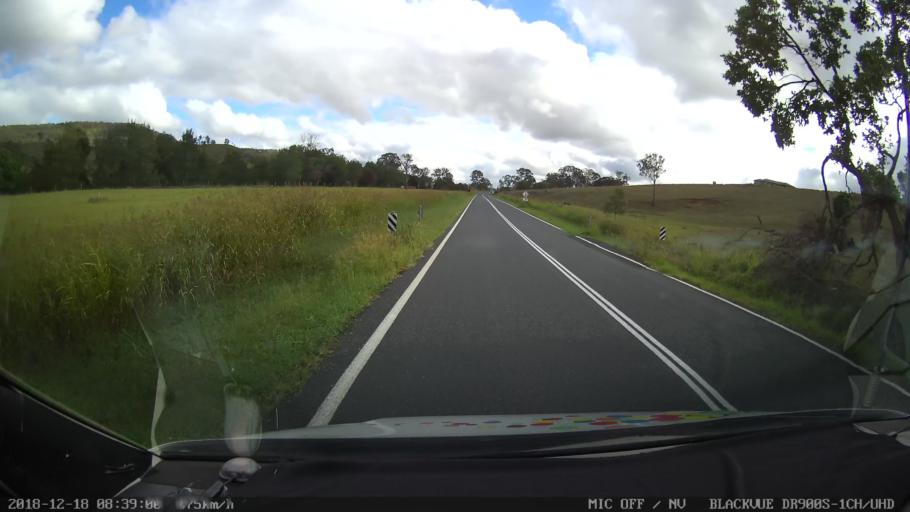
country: AU
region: New South Wales
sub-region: Kyogle
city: Kyogle
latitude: -28.2518
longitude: 152.8335
